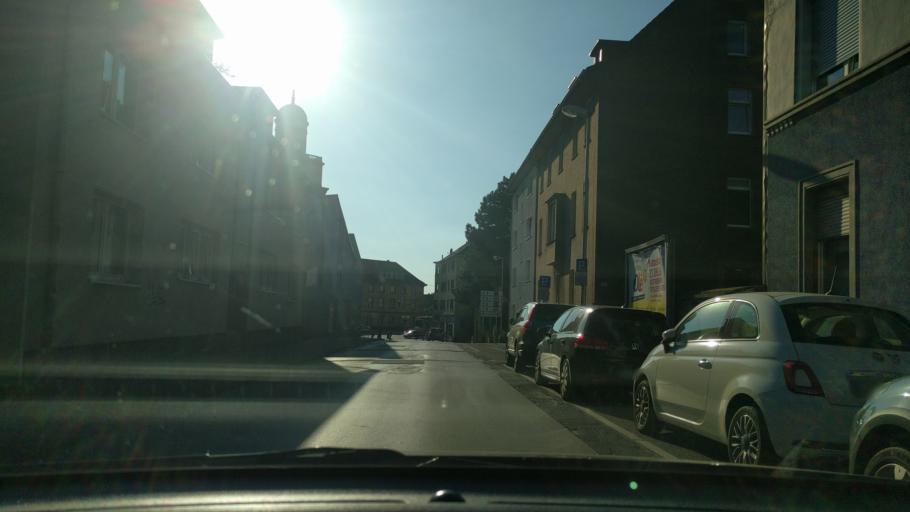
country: DE
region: North Rhine-Westphalia
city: Witten
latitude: 51.4404
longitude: 7.3379
